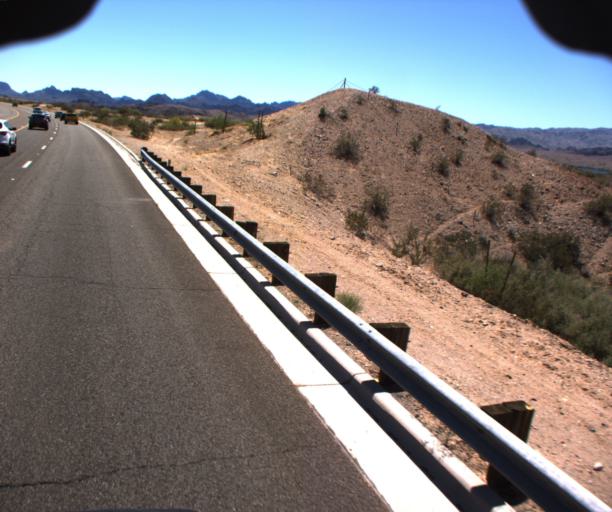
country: US
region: Arizona
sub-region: Mohave County
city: Lake Havasu City
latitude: 34.4589
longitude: -114.3313
